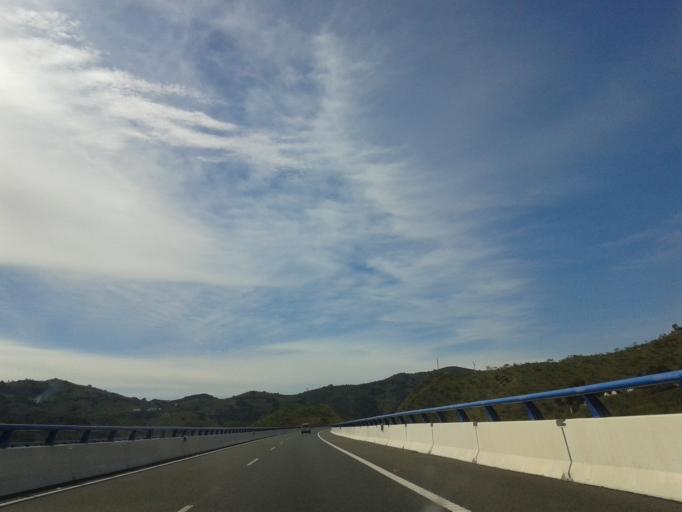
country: ES
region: Andalusia
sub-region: Provincia de Malaga
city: Casabermeja
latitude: 36.8892
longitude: -4.4690
